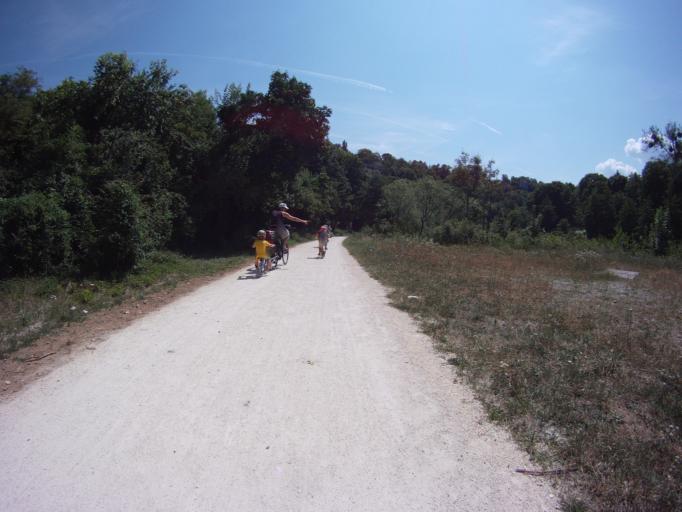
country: FR
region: Lorraine
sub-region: Departement de Meurthe-et-Moselle
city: Liverdun
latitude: 48.7569
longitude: 6.0612
